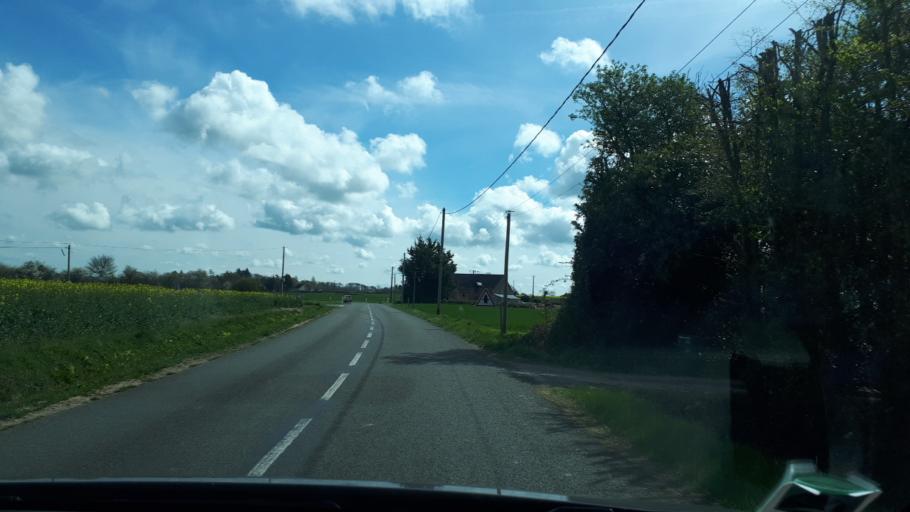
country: FR
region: Pays de la Loire
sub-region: Departement de la Sarthe
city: Bouloire
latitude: 47.8990
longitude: 0.6167
